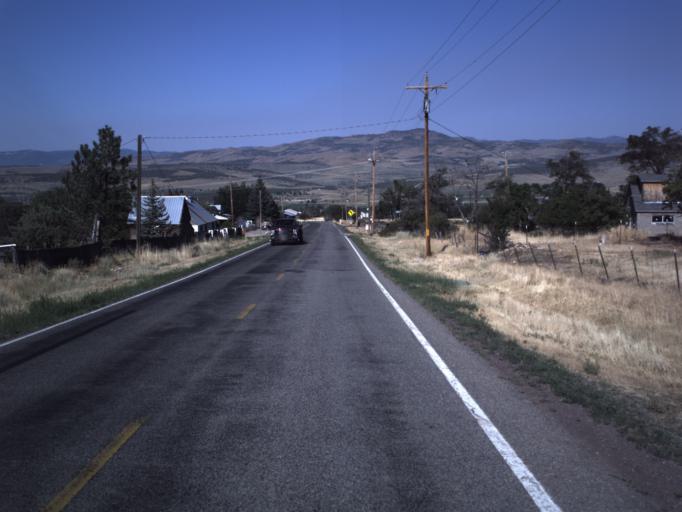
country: US
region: Utah
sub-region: Sanpete County
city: Fairview
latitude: 39.6432
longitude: -111.4136
